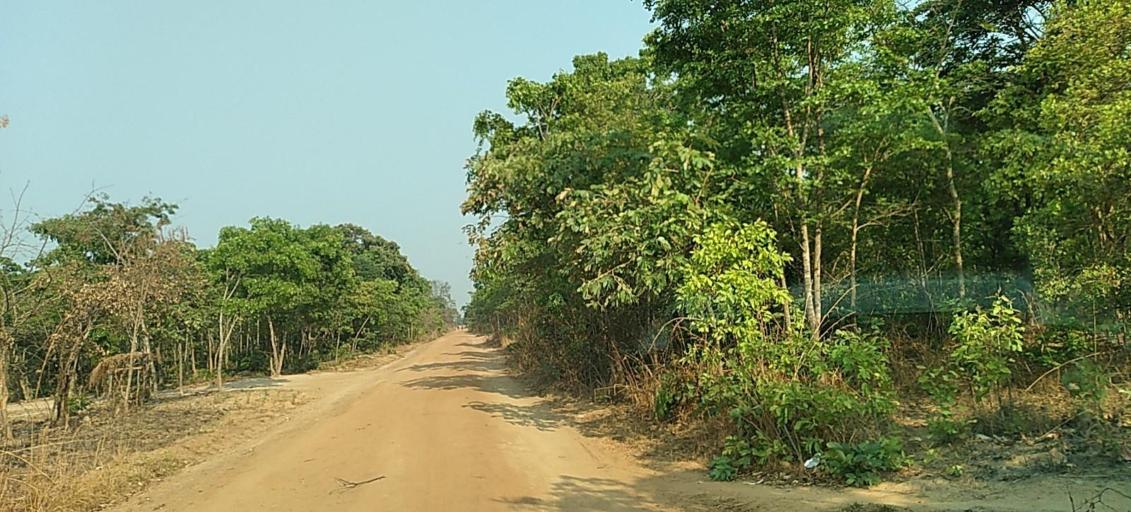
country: ZM
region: Copperbelt
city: Chingola
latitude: -12.8589
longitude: 27.5684
